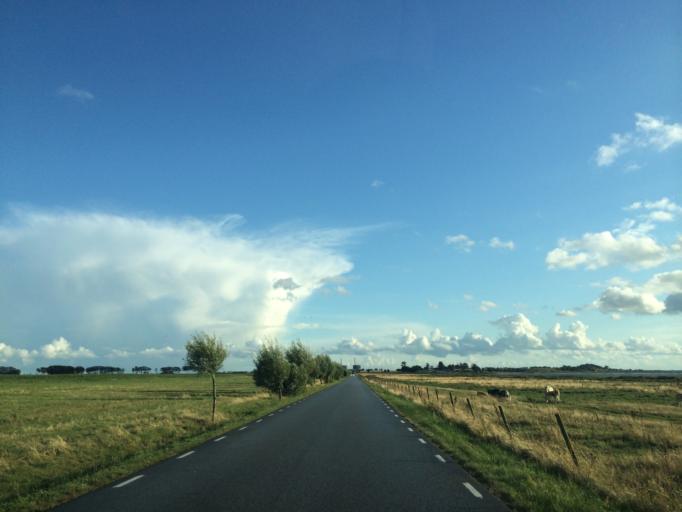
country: SE
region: Skane
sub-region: Kavlinge Kommun
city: Hofterup
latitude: 55.7817
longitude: 12.9357
